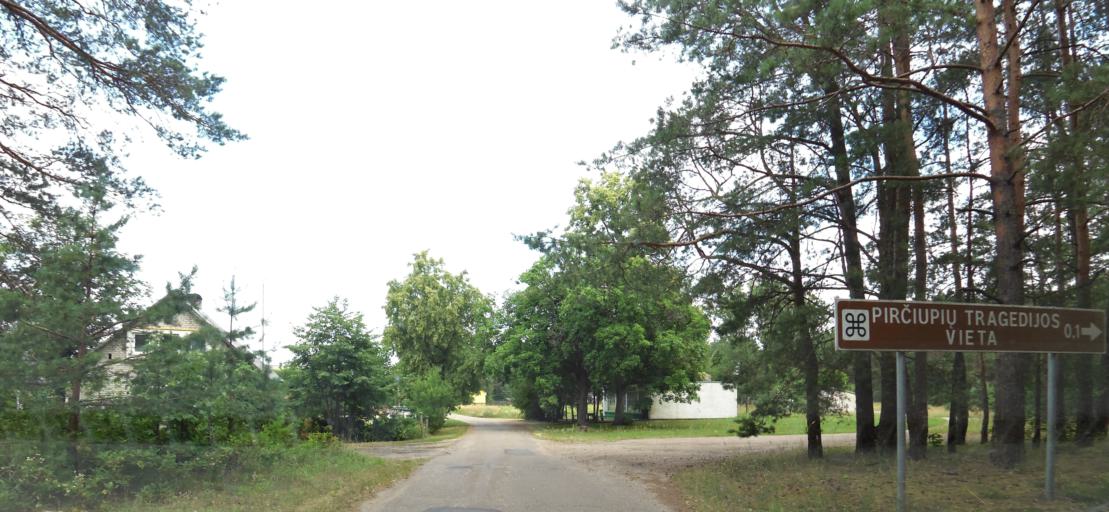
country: LT
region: Vilnius County
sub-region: Trakai
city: Rudiskes
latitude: 54.3976
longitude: 24.9582
